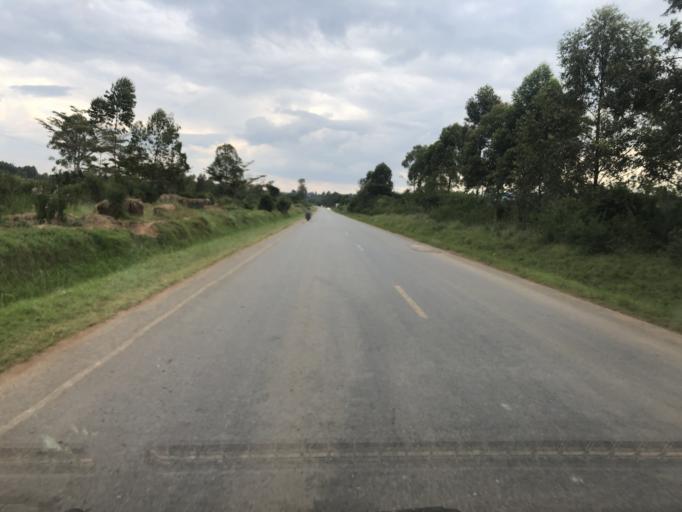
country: UG
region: Western Region
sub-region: Sheema District
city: Kibingo
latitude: -0.5797
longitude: 30.4273
